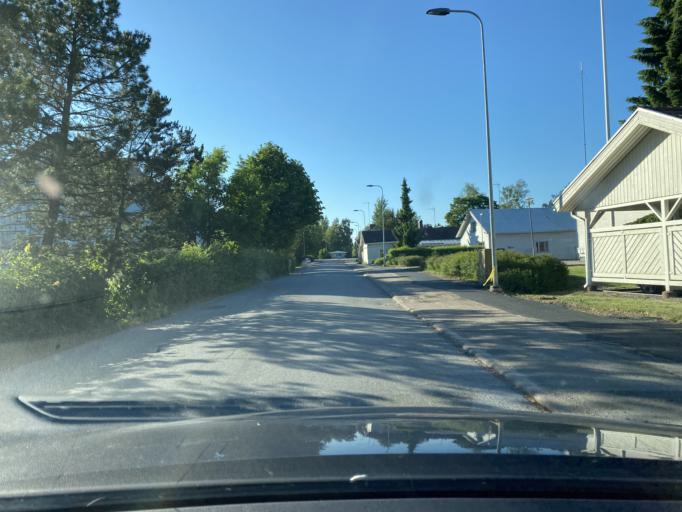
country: FI
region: Satakunta
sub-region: Pori
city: Huittinen
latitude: 61.1730
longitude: 22.6954
